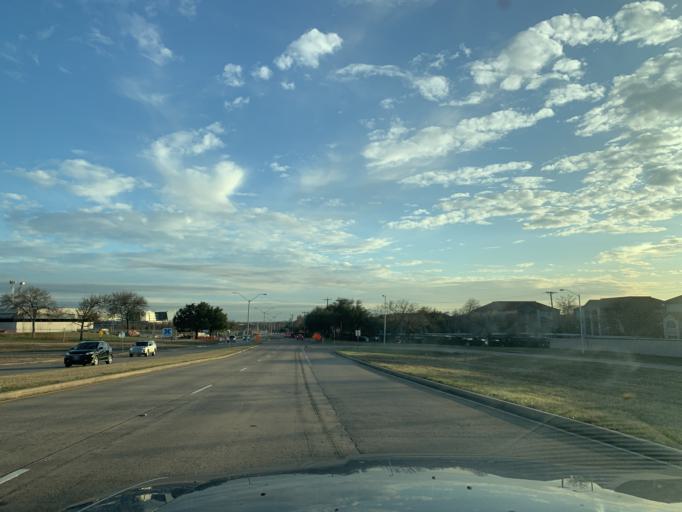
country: US
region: Texas
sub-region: Tarrant County
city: Euless
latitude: 32.8354
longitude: -97.0697
